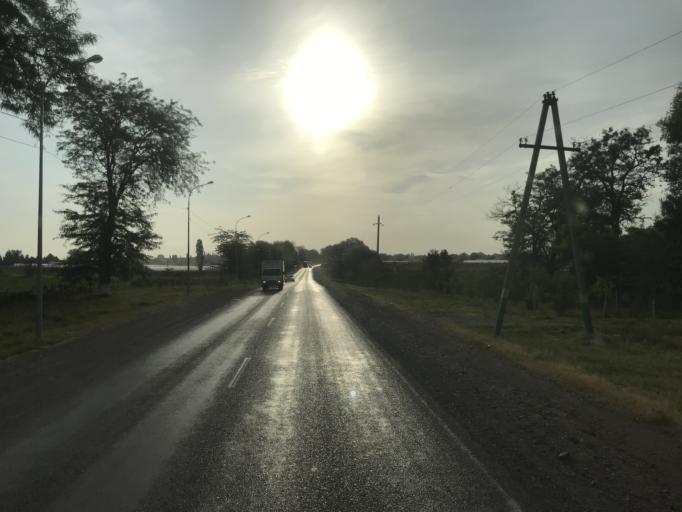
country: KZ
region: Ongtustik Qazaqstan
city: Saryaghash
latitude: 41.4923
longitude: 69.2935
